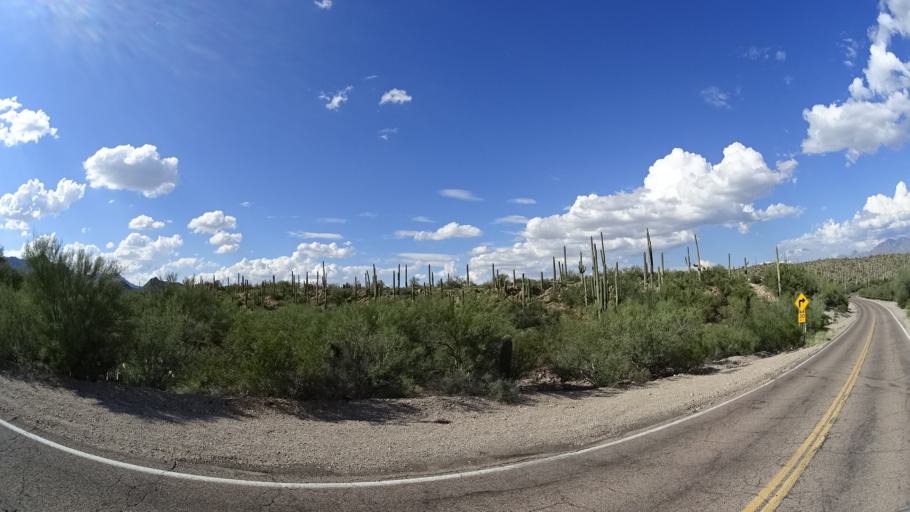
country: US
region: Arizona
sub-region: Pima County
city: Tucson Estates
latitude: 32.2373
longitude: -111.0523
